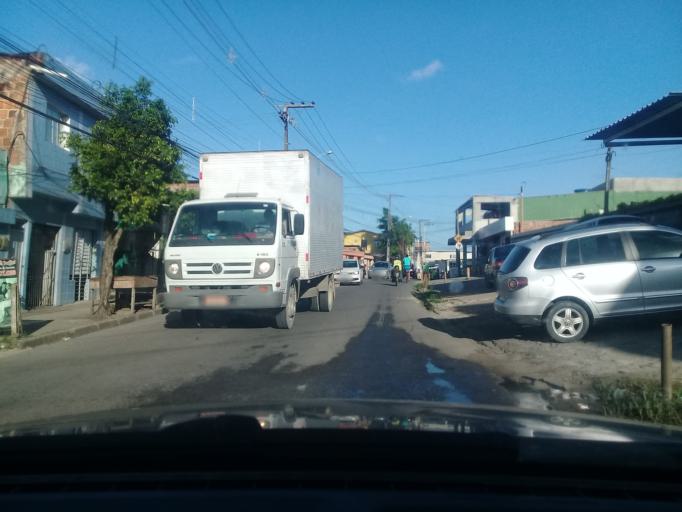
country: BR
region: Pernambuco
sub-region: Jaboatao Dos Guararapes
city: Jaboatao dos Guararapes
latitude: -8.1098
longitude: -34.9615
